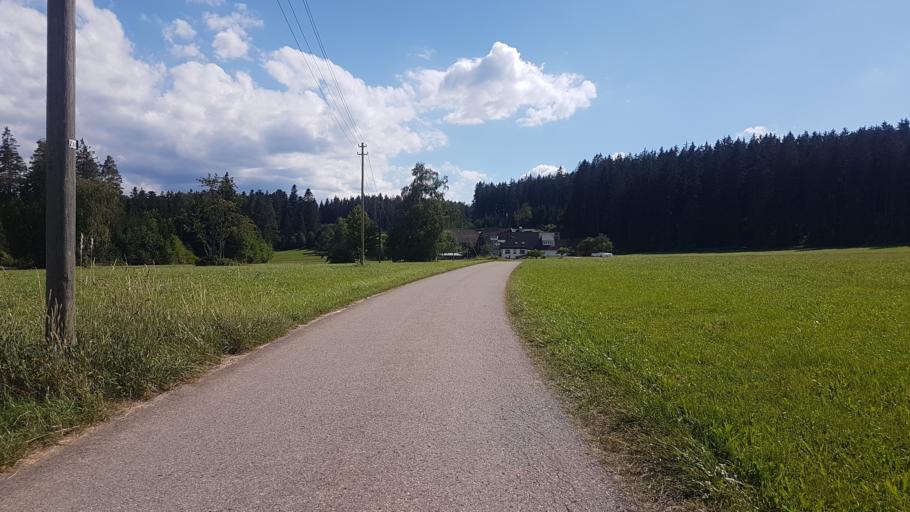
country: DE
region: Baden-Wuerttemberg
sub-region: Freiburg Region
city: Konigsfeld im Schwarzwald
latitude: 48.1390
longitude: 8.4016
